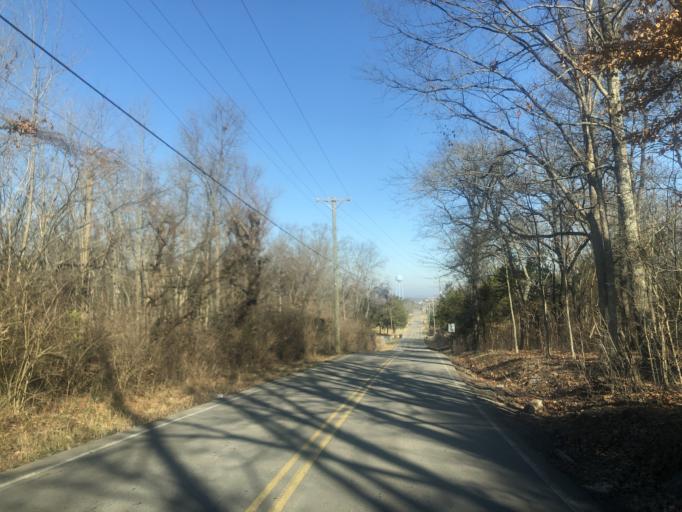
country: US
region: Tennessee
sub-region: Rutherford County
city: La Vergne
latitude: 36.0070
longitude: -86.5832
